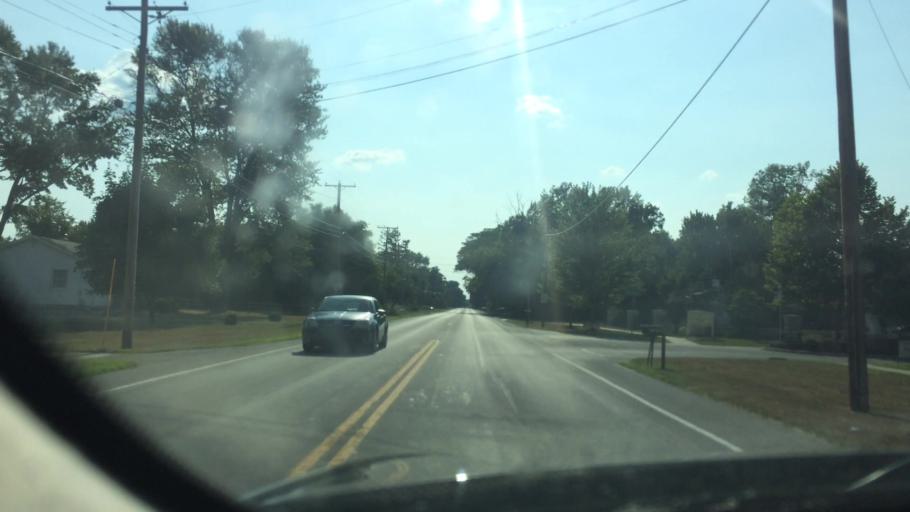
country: US
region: Ohio
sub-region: Lucas County
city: Holland
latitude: 41.6540
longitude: -83.7132
